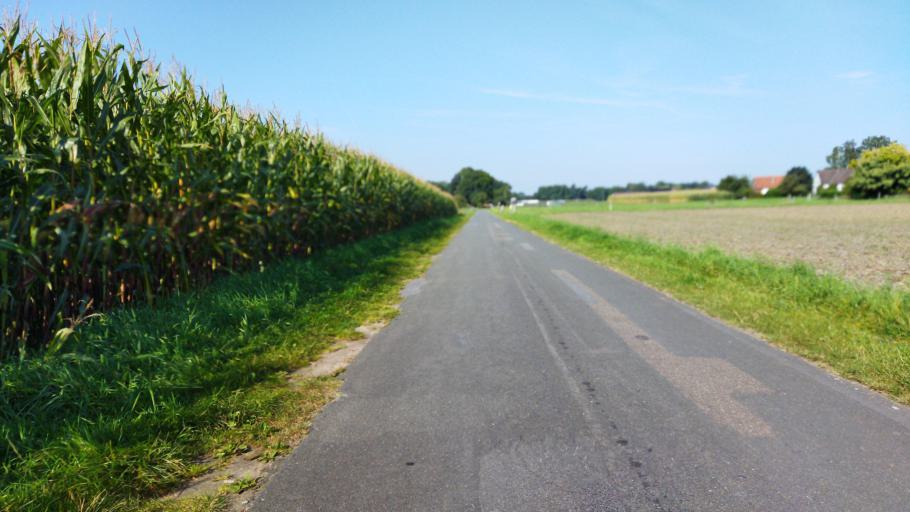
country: DE
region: North Rhine-Westphalia
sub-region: Regierungsbezirk Munster
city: Lienen
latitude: 52.1442
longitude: 7.9572
